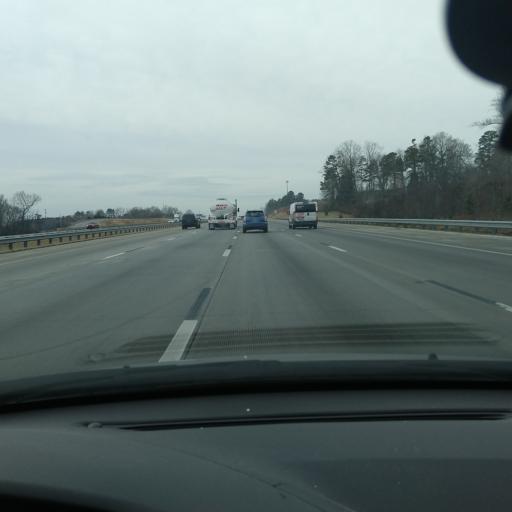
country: US
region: North Carolina
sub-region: Davidson County
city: Tyro
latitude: 35.7445
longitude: -80.3585
